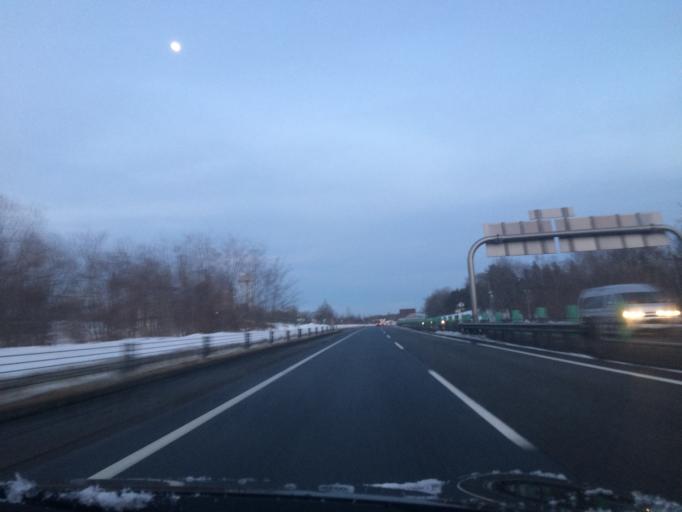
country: JP
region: Hokkaido
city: Chitose
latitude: 42.8428
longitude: 141.5930
